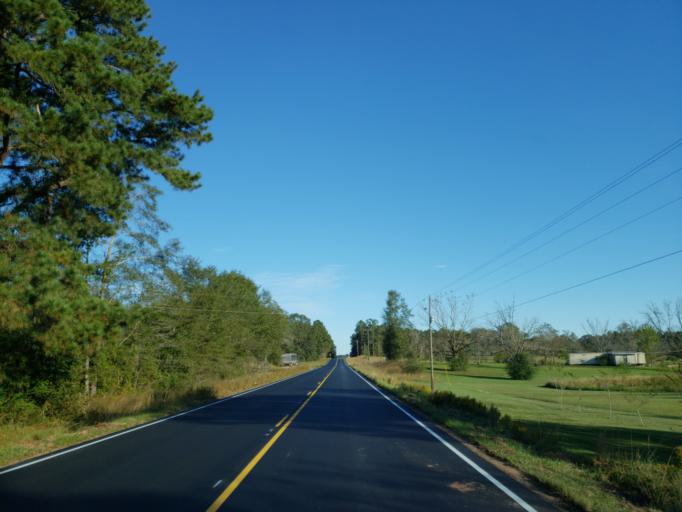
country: US
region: Mississippi
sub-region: Perry County
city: Richton
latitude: 31.3713
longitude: -88.8237
